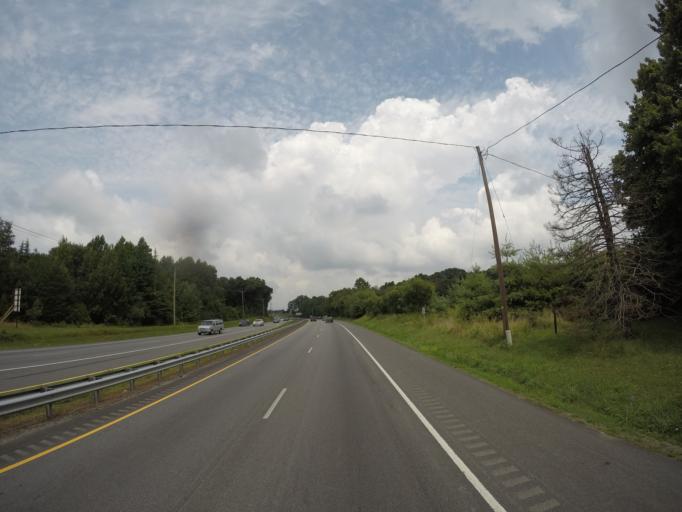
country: US
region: Maryland
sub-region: Queen Anne's County
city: Centreville
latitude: 38.9476
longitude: -76.0646
